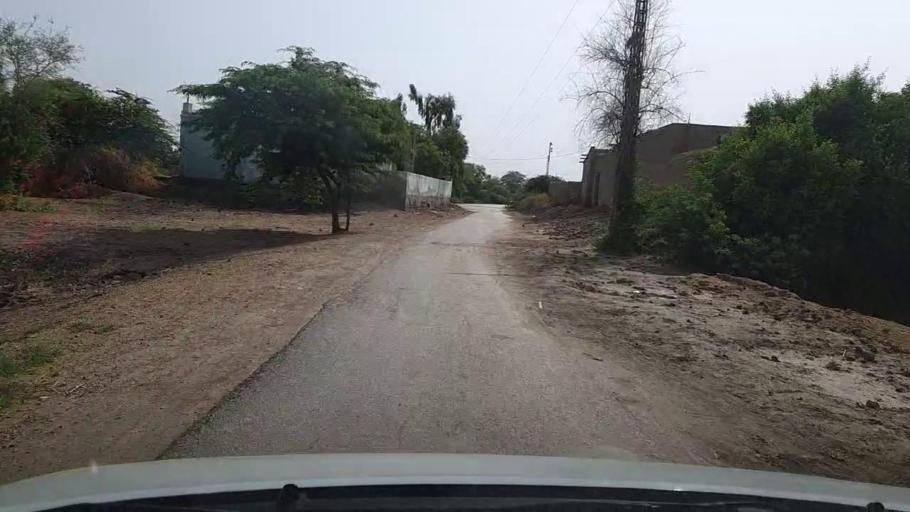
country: PK
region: Sindh
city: Mehar
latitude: 27.1207
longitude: 67.8464
